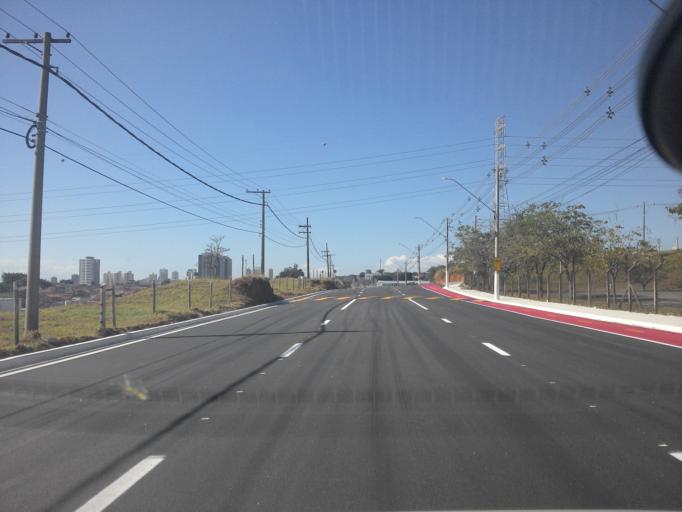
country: BR
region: Sao Paulo
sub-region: Taubate
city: Taubate
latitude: -23.0482
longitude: -45.5950
